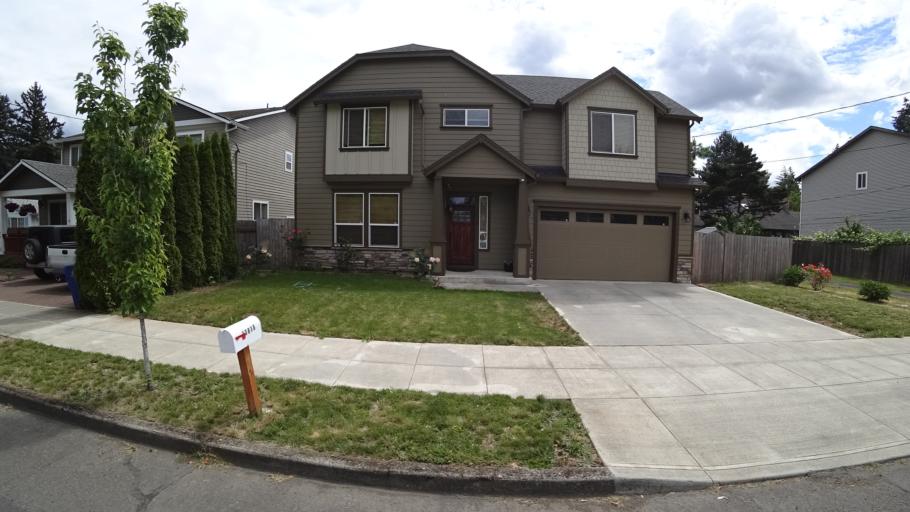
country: US
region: Oregon
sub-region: Clackamas County
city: Happy Valley
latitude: 45.4933
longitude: -122.5211
